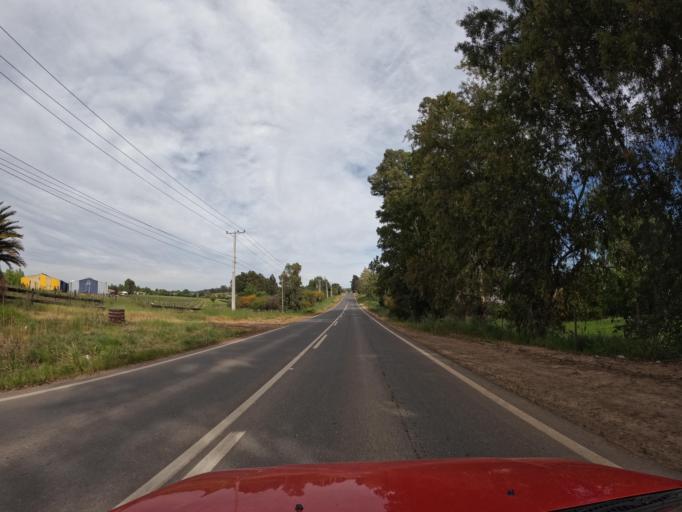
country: CL
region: Maule
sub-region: Provincia de Talca
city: Talca
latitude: -35.3875
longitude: -71.8171
